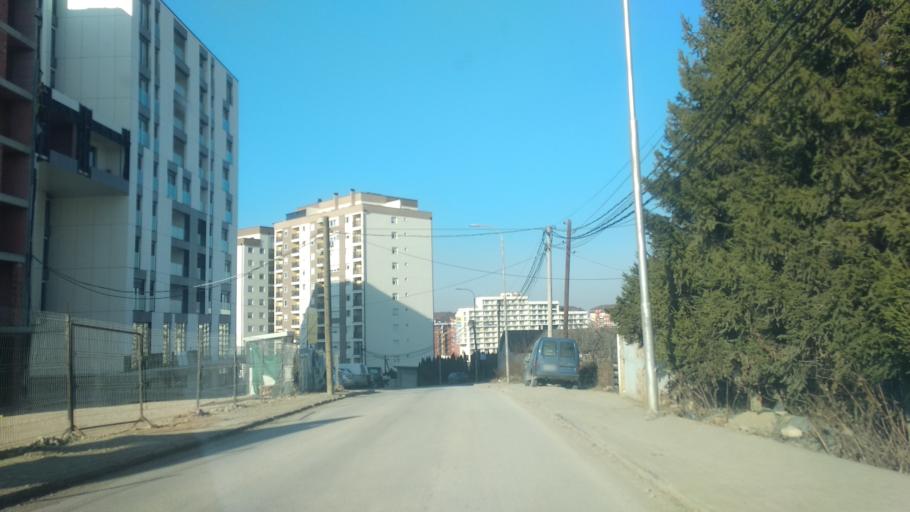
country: XK
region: Pristina
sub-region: Komuna e Prishtines
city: Pristina
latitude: 42.6397
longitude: 21.1587
